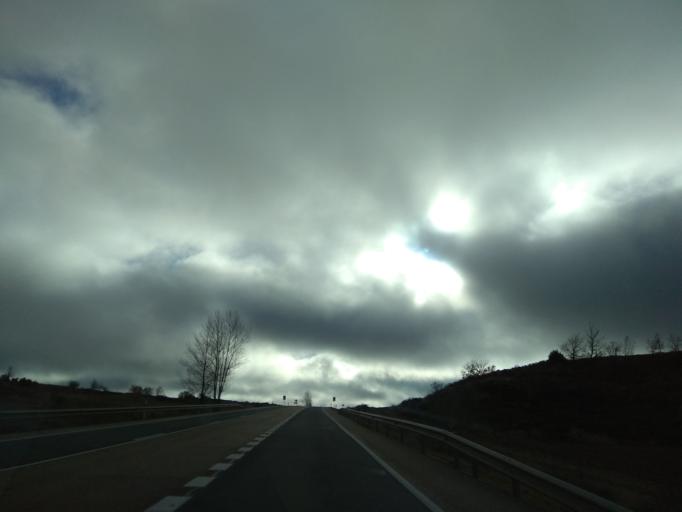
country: ES
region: Castille and Leon
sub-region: Provincia de Burgos
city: Huermeces
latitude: 42.5509
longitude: -3.7427
